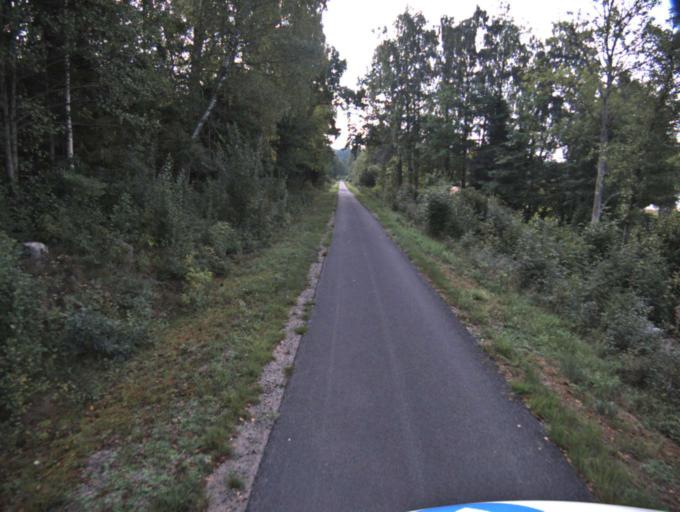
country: SE
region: Vaestra Goetaland
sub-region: Ulricehamns Kommun
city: Ulricehamn
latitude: 57.7126
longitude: 13.3945
